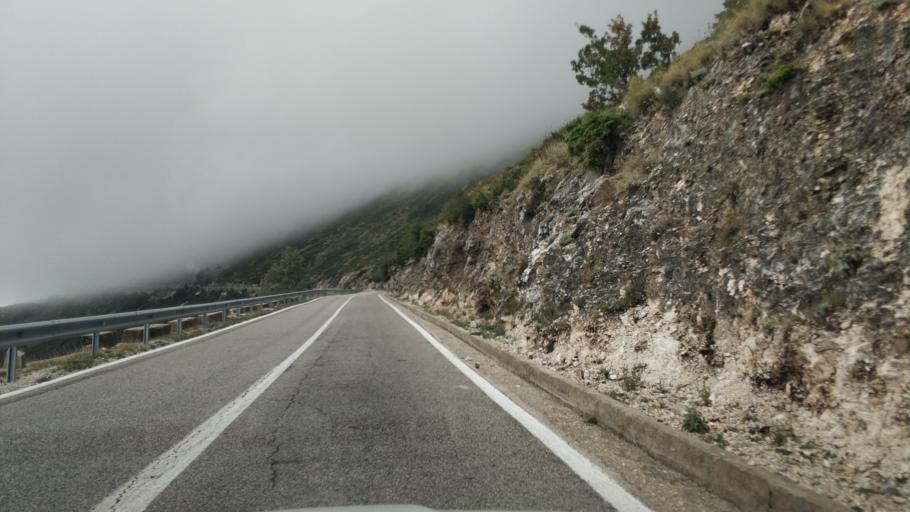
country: AL
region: Vlore
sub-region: Rrethi i Vlores
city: Vranisht
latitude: 40.1907
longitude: 19.6073
